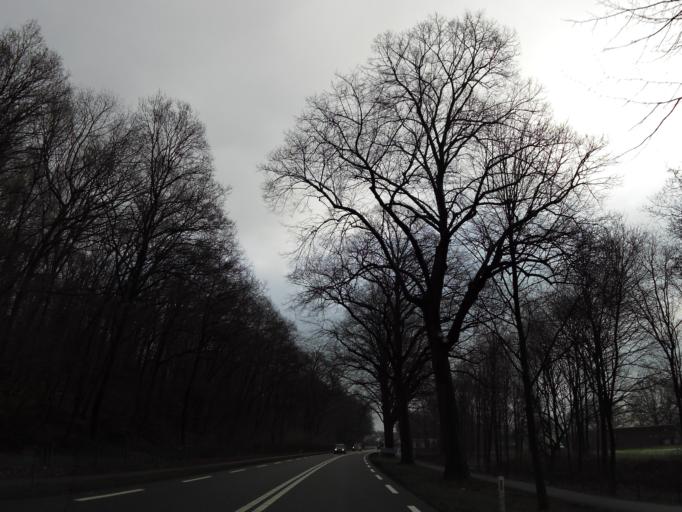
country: NL
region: North Brabant
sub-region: Gemeente Cuijk
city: Cuijk
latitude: 51.7402
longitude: 5.9130
